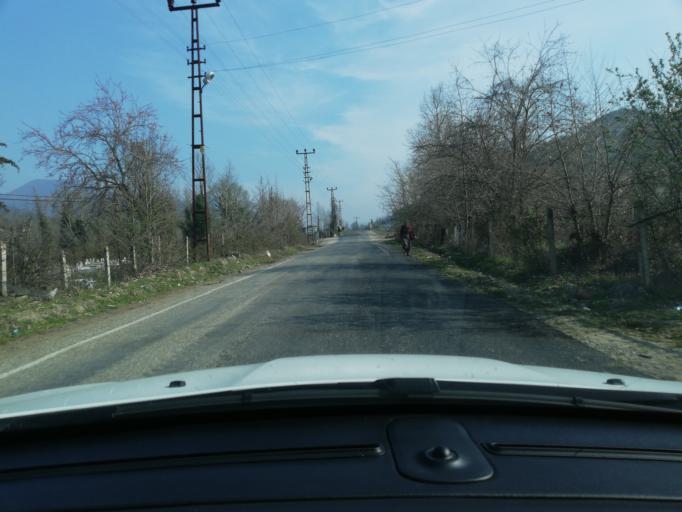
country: TR
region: Karabuk
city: Yenice
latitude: 41.2455
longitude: 32.3563
